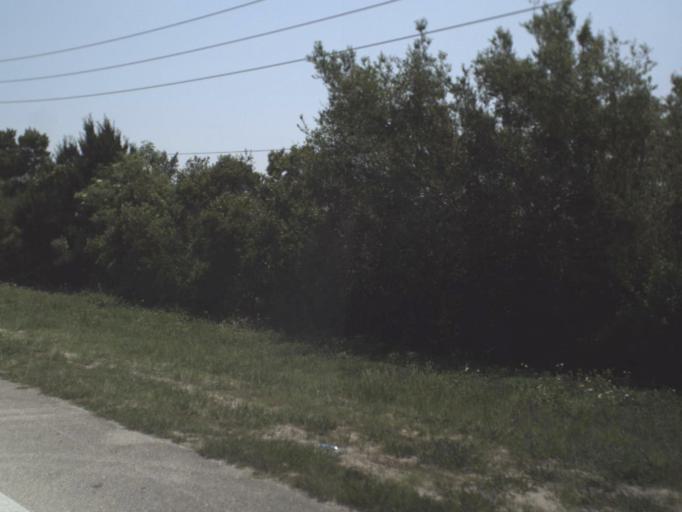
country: US
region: Florida
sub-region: Saint Johns County
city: Butler Beach
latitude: 29.7602
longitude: -81.2684
